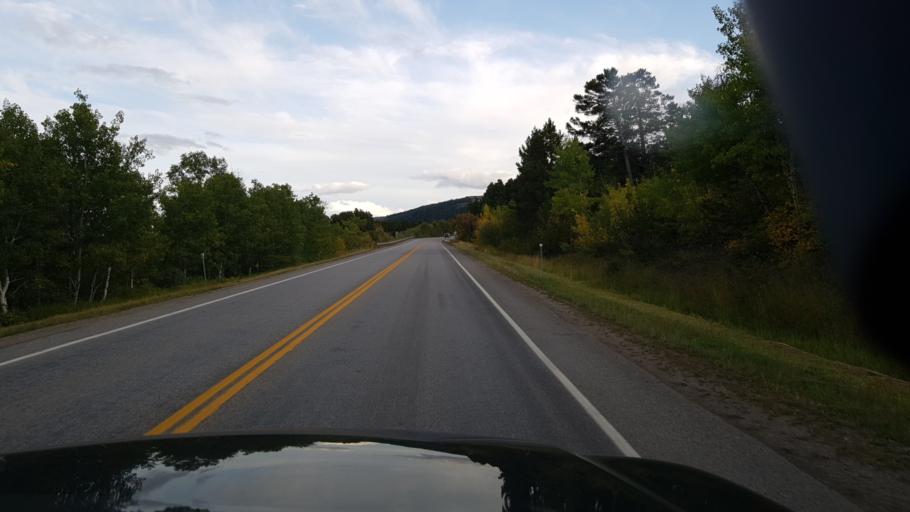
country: US
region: Montana
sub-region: Glacier County
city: South Browning
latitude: 48.4369
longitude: -113.2171
